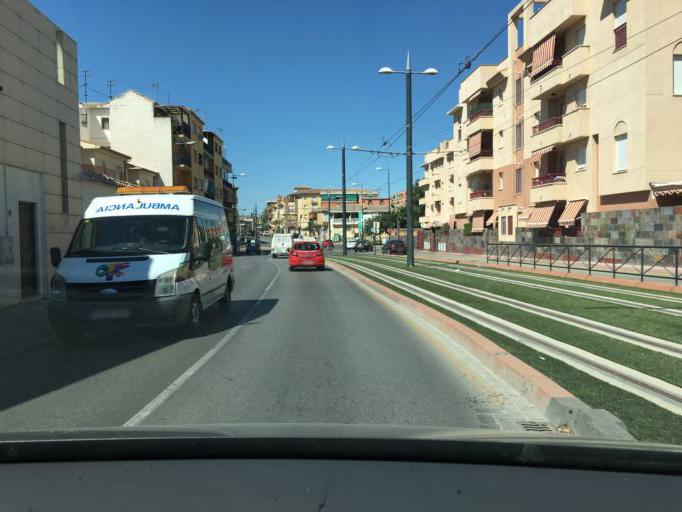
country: ES
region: Andalusia
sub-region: Provincia de Granada
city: Maracena
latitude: 37.2049
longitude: -3.6276
